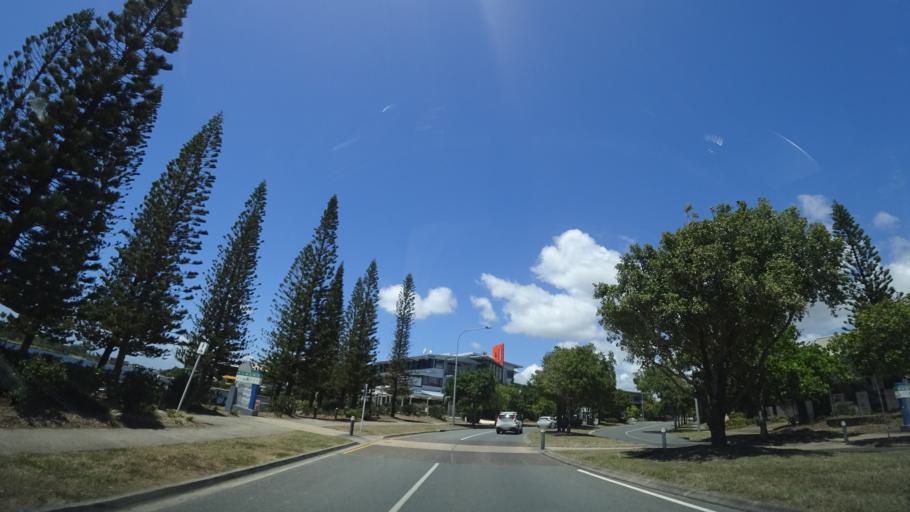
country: AU
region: Queensland
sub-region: Sunshine Coast
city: Mooloolaba
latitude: -26.7312
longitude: 153.1226
